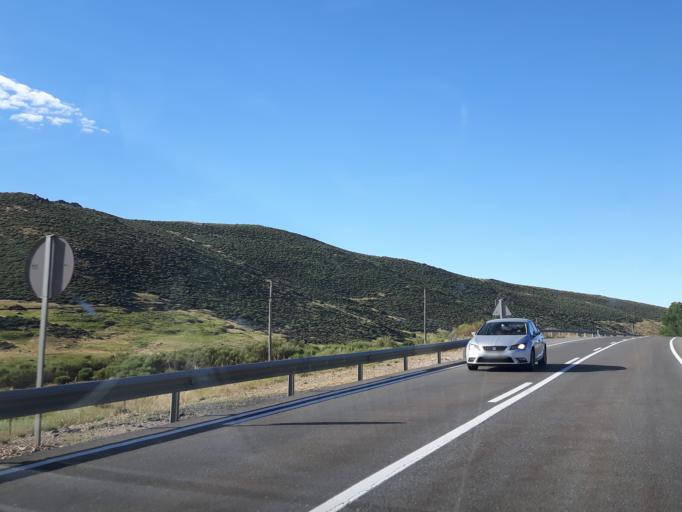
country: ES
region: Castille and Leon
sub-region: Provincia de Avila
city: Mengamunoz
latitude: 40.4725
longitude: -5.0158
